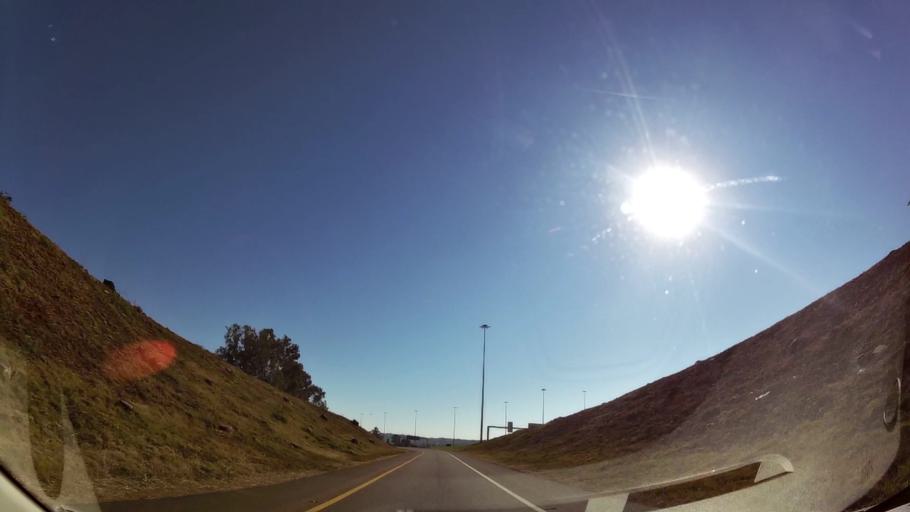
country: ZA
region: Gauteng
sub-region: City of Tshwane Metropolitan Municipality
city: Centurion
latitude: -25.8282
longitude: 28.2417
